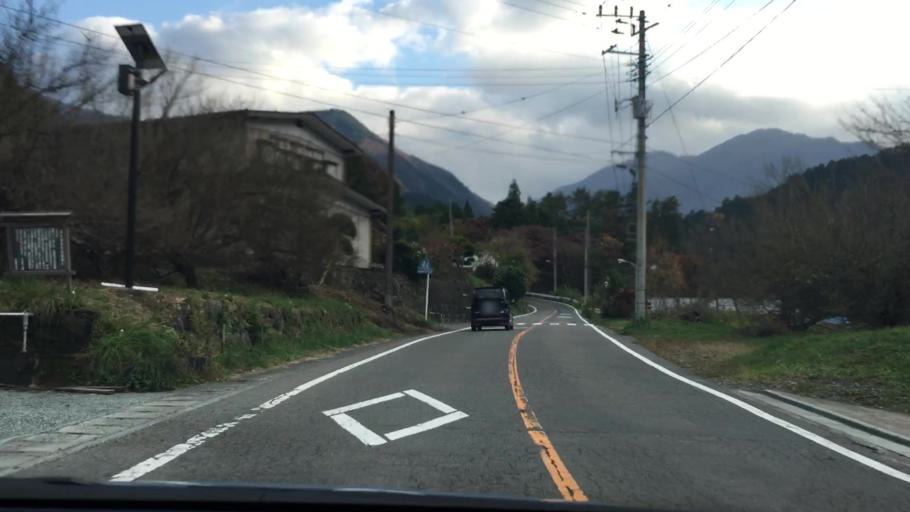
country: JP
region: Yamanashi
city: Uenohara
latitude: 35.5303
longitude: 139.0964
